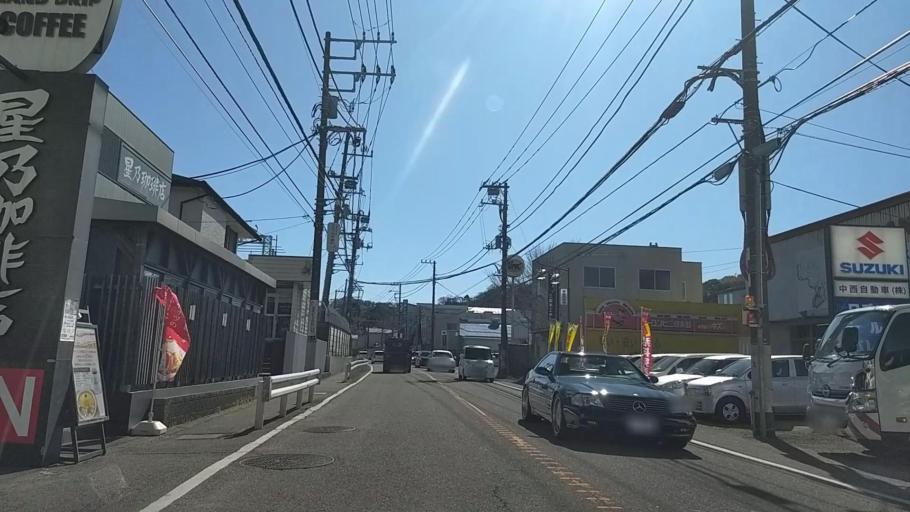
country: JP
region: Kanagawa
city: Kamakura
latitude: 35.3253
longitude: 139.5243
